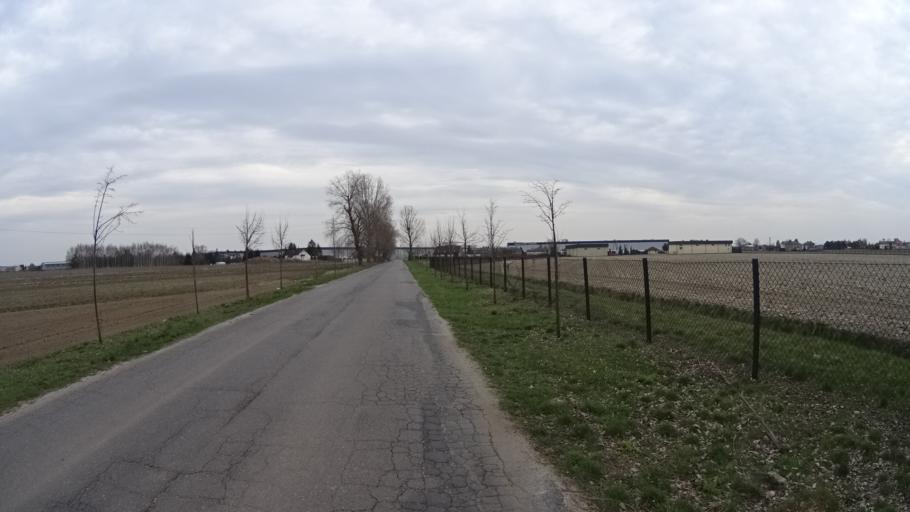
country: PL
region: Masovian Voivodeship
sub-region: Powiat pruszkowski
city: Piastow
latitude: 52.2026
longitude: 20.8244
